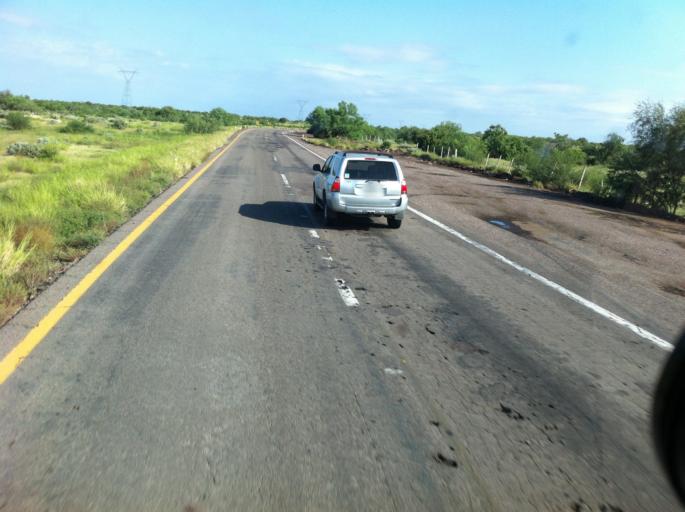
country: MX
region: Sonora
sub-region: Hermosillo
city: Miguel Aleman (La Doce)
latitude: 28.5236
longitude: -111.0468
